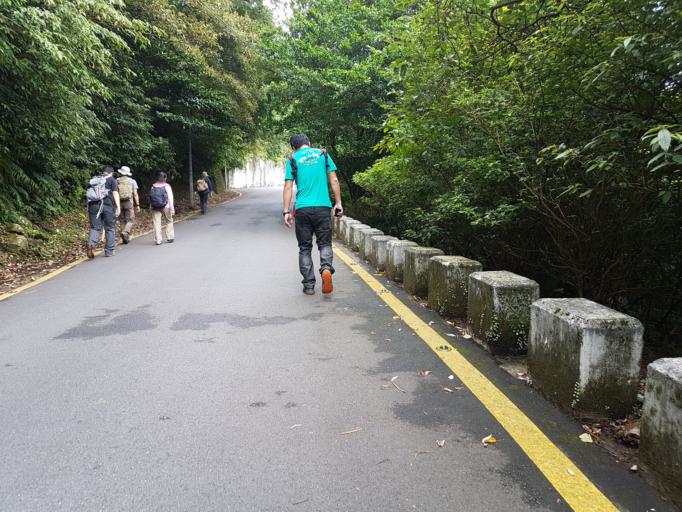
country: TW
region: Taiwan
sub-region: Keelung
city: Keelung
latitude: 25.0514
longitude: 121.6650
